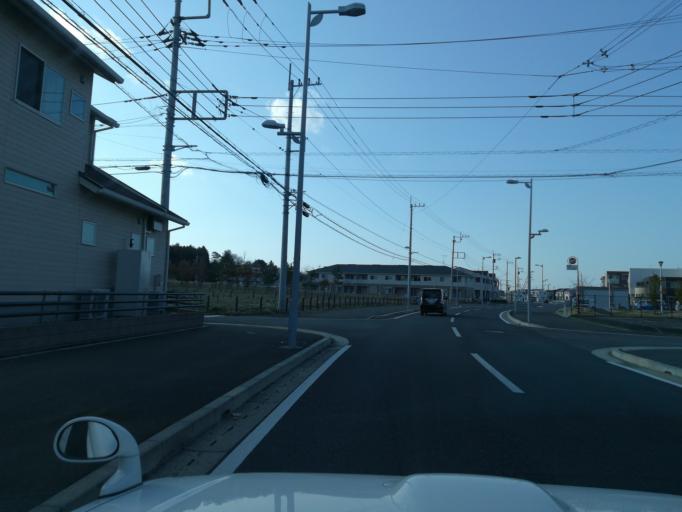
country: JP
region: Ibaraki
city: Naka
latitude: 36.0942
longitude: 140.0894
